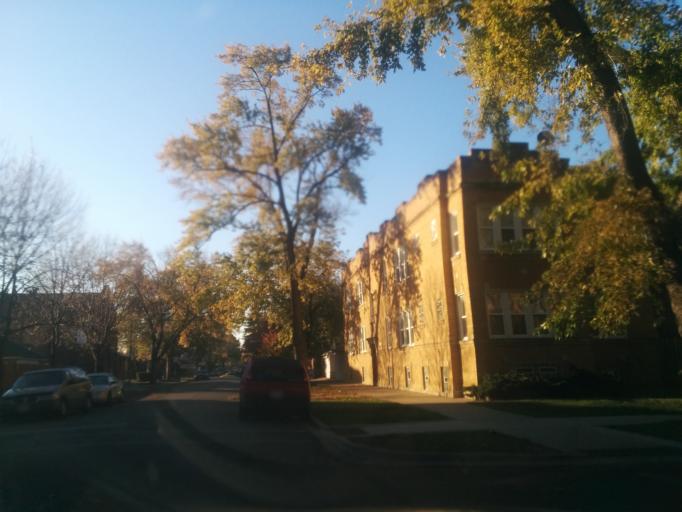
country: US
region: Illinois
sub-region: Cook County
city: Elmwood Park
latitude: 41.9343
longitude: -87.7517
